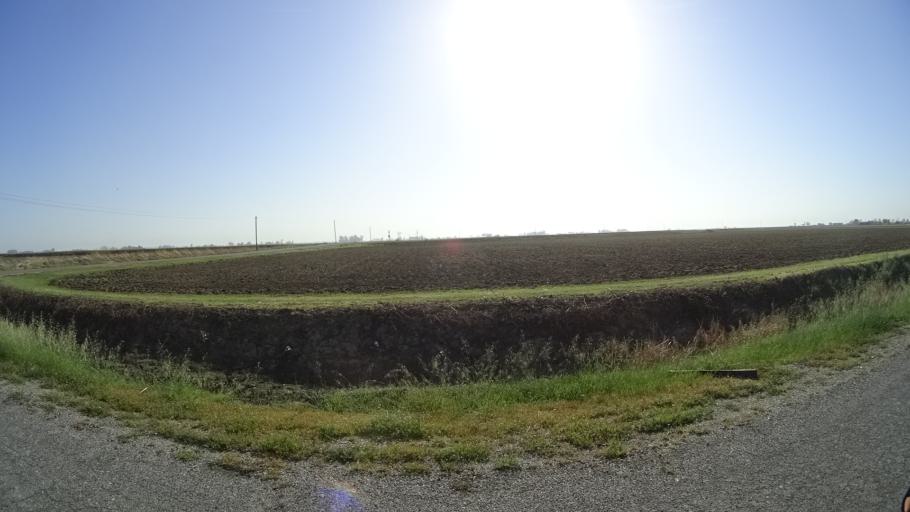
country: US
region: California
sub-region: Glenn County
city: Willows
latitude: 39.5530
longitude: -122.1321
